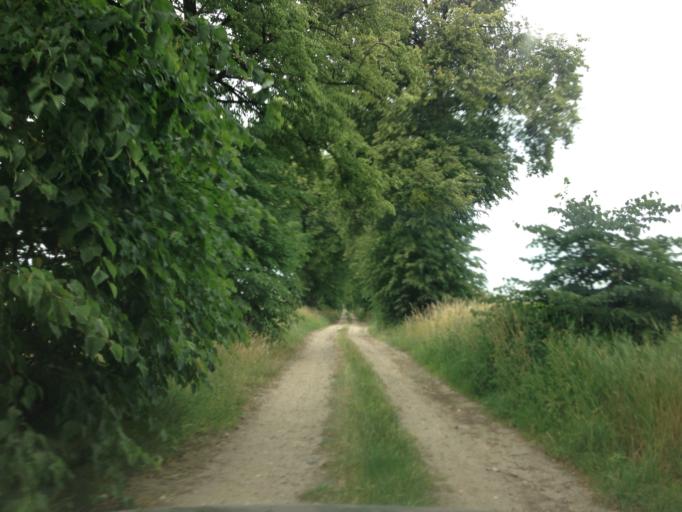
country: PL
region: Kujawsko-Pomorskie
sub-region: Powiat rypinski
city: Wapielsk
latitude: 53.2099
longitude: 19.2508
